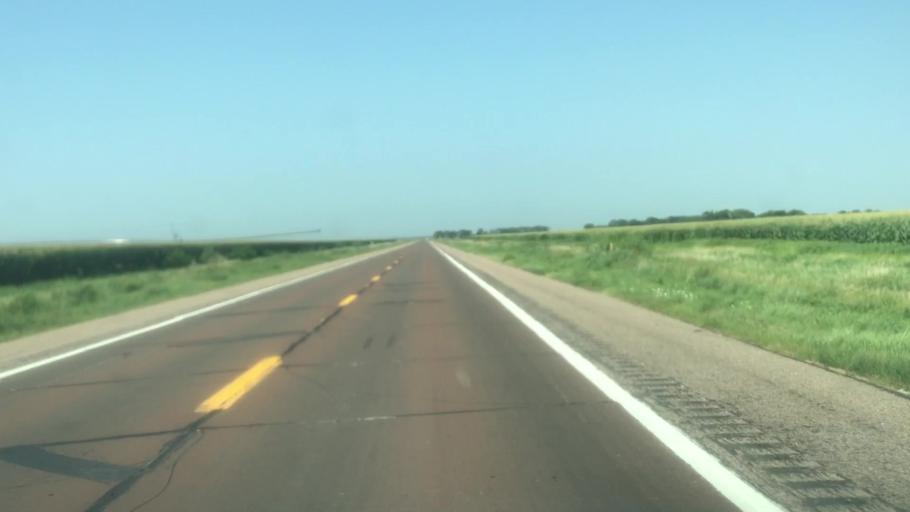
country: US
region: Nebraska
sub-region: Hall County
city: Grand Island
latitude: 40.9677
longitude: -98.4850
